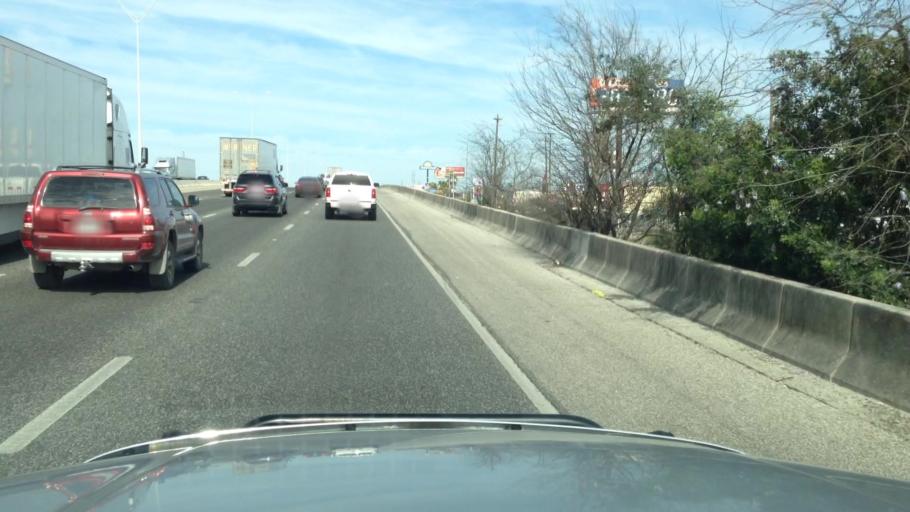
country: US
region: Texas
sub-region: Bexar County
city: Windcrest
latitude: 29.5385
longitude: -98.3799
